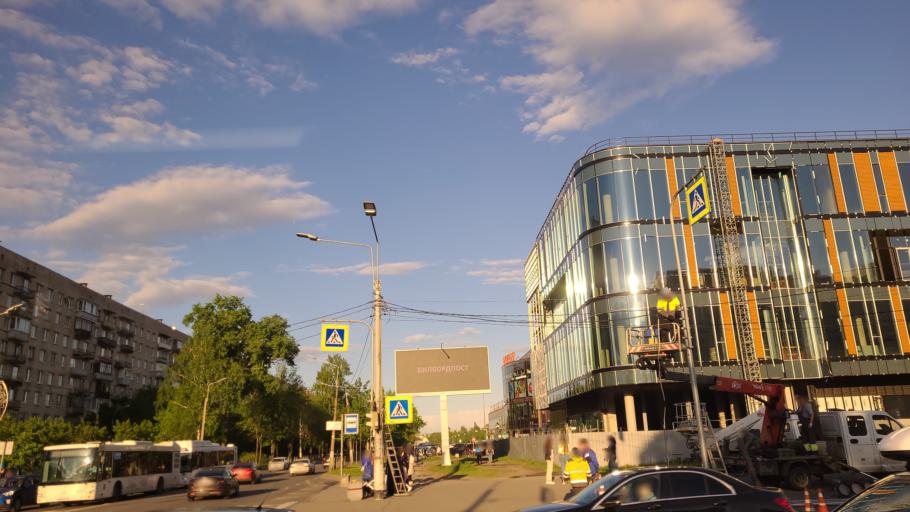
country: RU
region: St.-Petersburg
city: Kolpino
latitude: 59.7414
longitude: 30.5811
